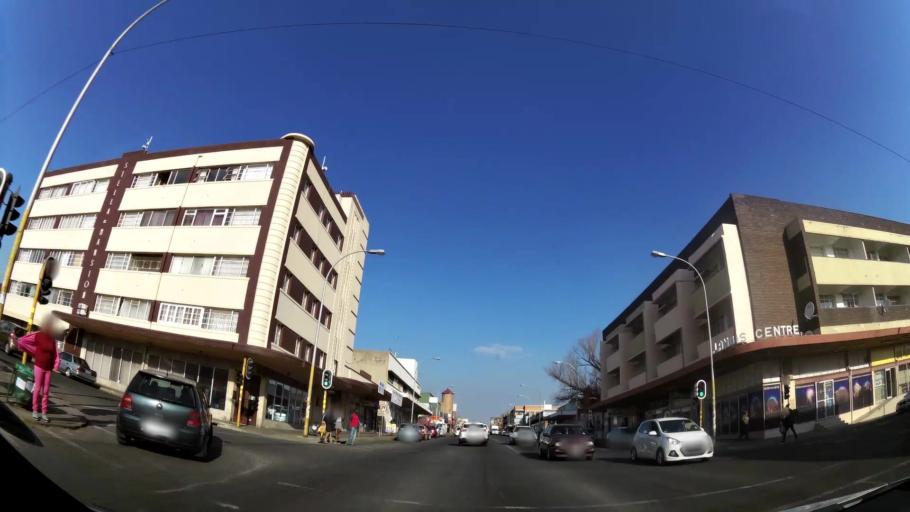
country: ZA
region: Gauteng
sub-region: Ekurhuleni Metropolitan Municipality
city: Brakpan
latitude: -26.2386
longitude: 28.3655
